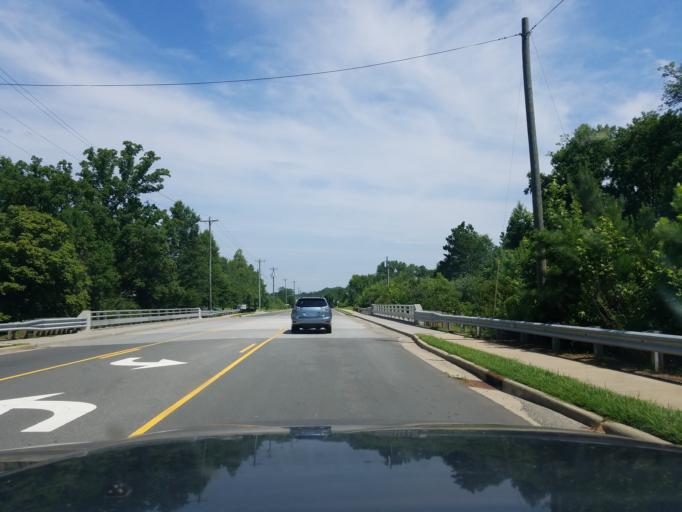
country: US
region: North Carolina
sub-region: Durham County
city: Durham
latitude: 35.9547
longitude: -78.9726
